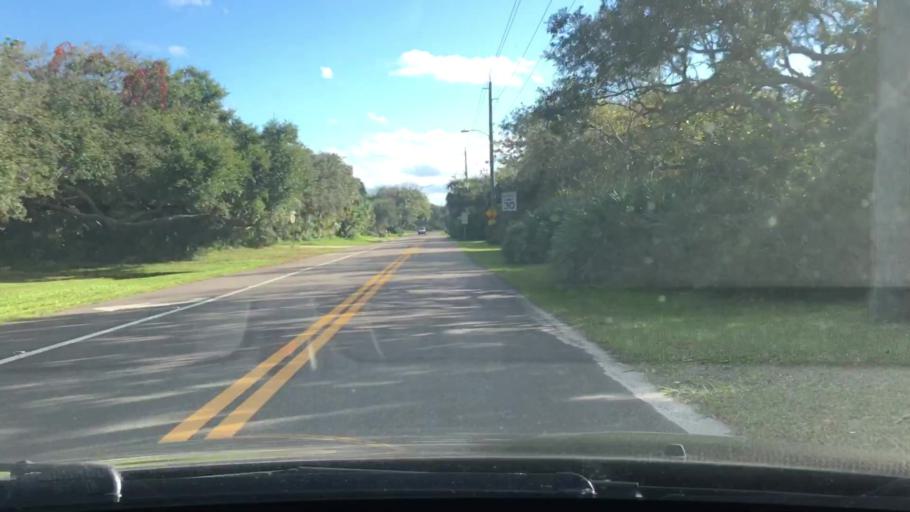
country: US
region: Florida
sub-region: Volusia County
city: Ormond-by-the-Sea
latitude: 29.3814
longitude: -81.0868
